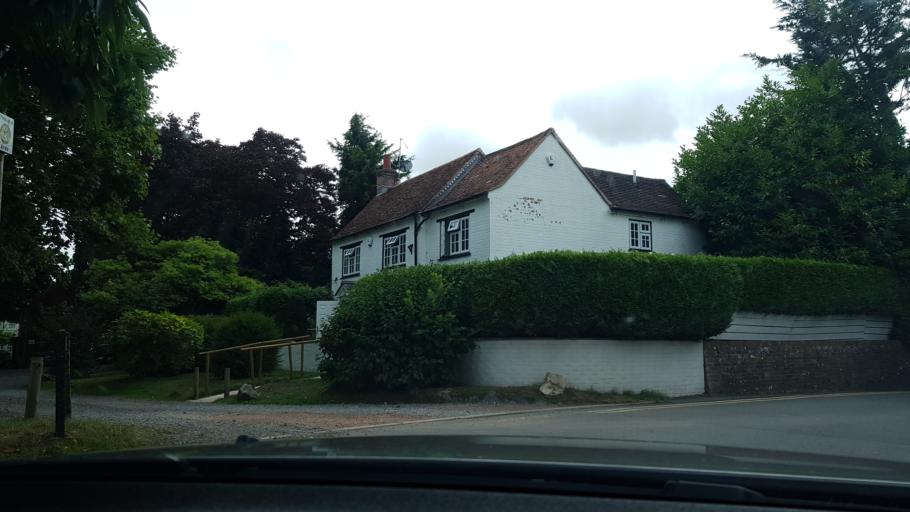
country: GB
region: England
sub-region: West Berkshire
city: Hungerford
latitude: 51.4156
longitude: -1.5189
